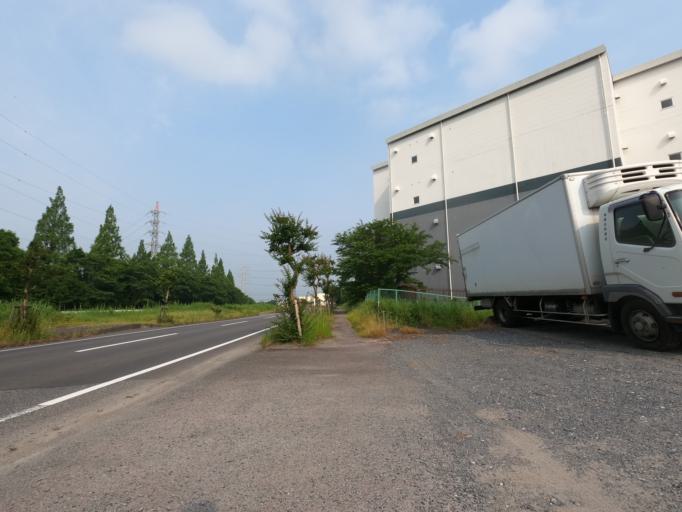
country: JP
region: Ibaraki
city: Moriya
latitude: 35.9565
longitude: 139.9604
